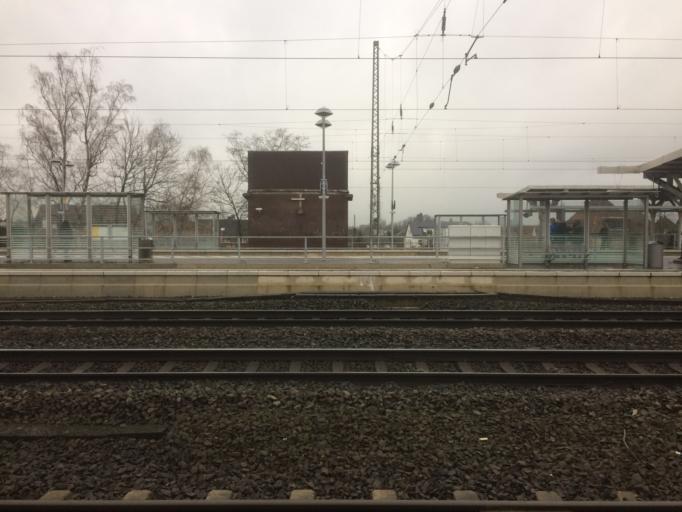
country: DE
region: North Rhine-Westphalia
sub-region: Regierungsbezirk Detmold
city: Rheda-Wiedenbruck
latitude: 51.8570
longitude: 8.2860
